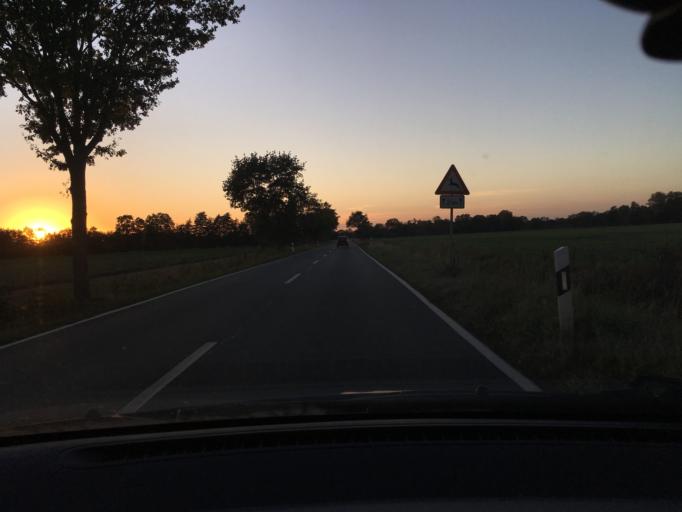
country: DE
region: Lower Saxony
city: Hittbergen
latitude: 53.3162
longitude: 10.6236
